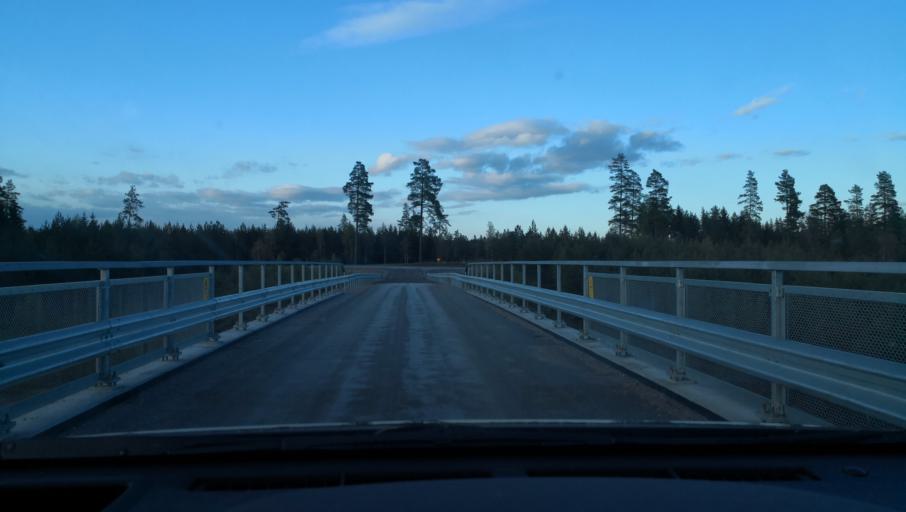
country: SE
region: OErebro
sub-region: Askersunds Kommun
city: Asbro
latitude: 58.8989
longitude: 15.1038
